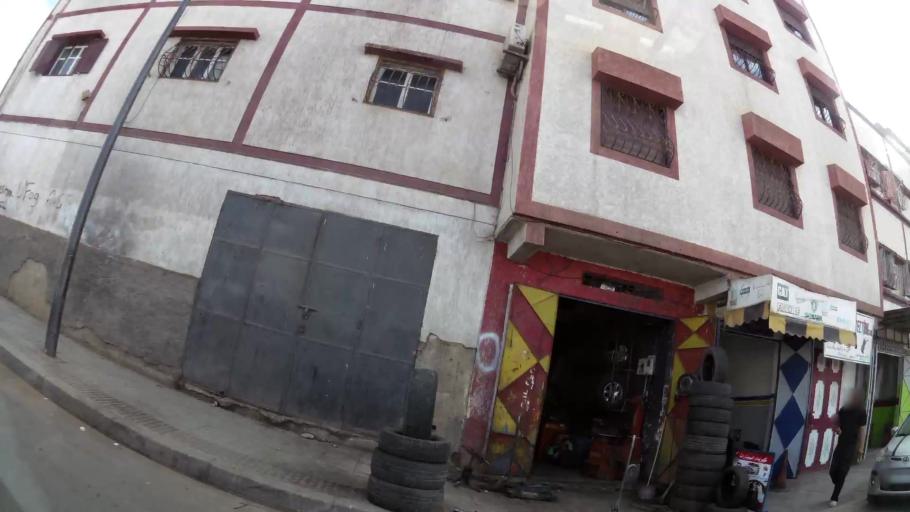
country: MA
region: Rabat-Sale-Zemmour-Zaer
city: Sale
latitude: 34.0543
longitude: -6.7731
